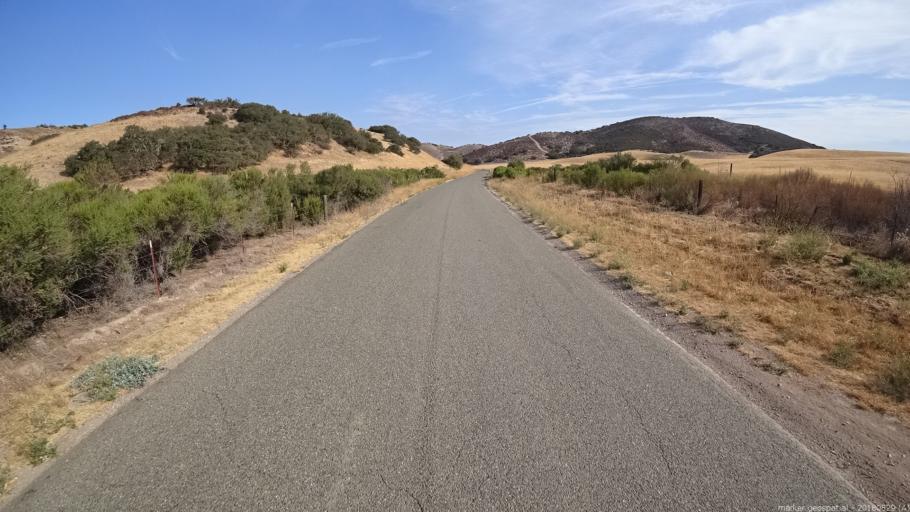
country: US
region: California
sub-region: Monterey County
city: King City
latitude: 36.0496
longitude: -121.0523
